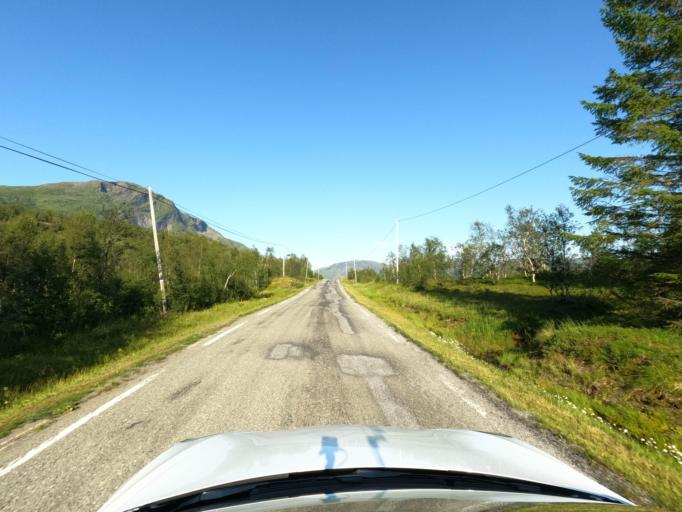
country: NO
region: Nordland
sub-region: Narvik
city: Bjerkvik
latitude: 68.5584
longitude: 17.6487
